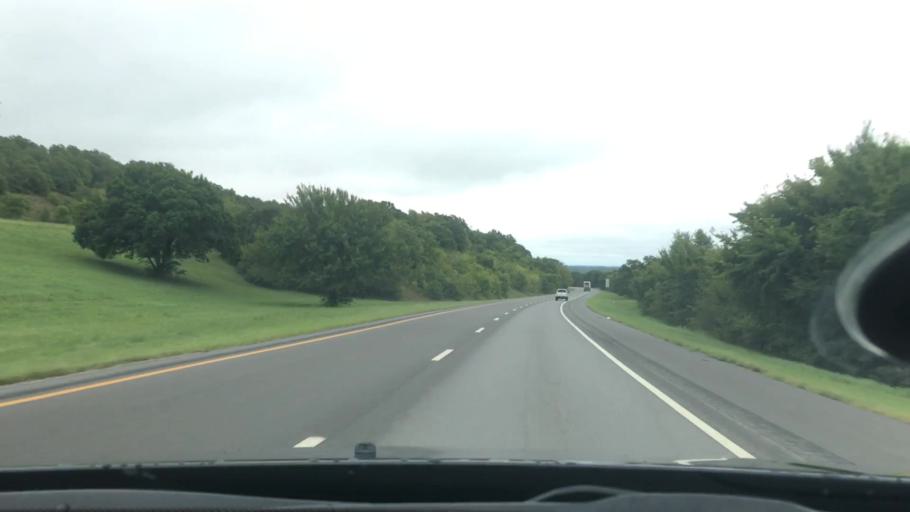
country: US
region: Oklahoma
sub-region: Okmulgee County
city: Morris
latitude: 35.4411
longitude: -95.7810
